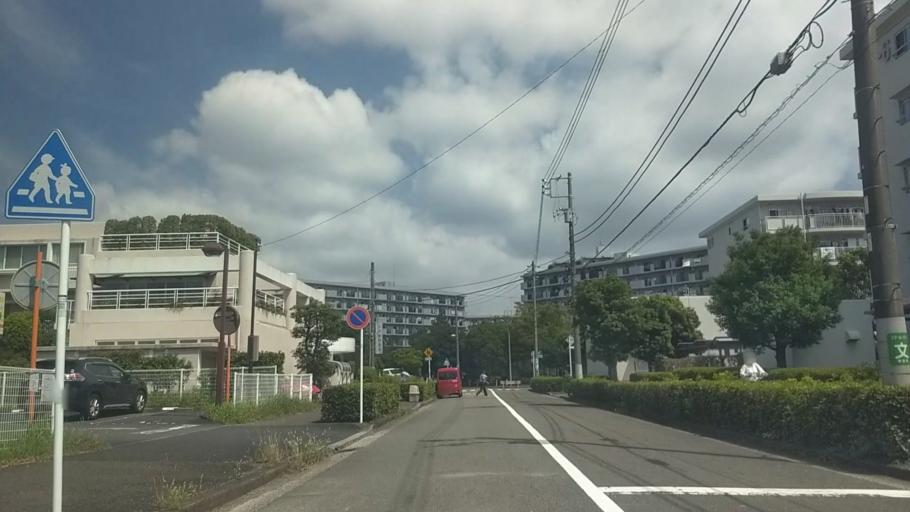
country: JP
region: Kanagawa
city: Yokohama
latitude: 35.3636
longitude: 139.6407
